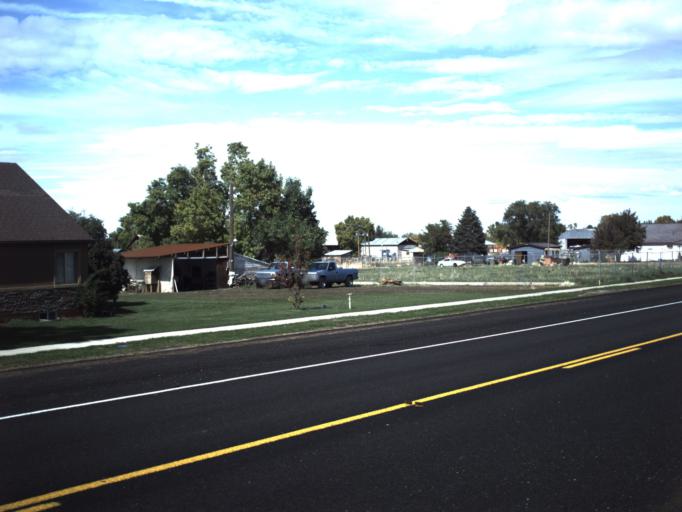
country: US
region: Utah
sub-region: Millard County
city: Fillmore
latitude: 38.7954
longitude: -112.4376
